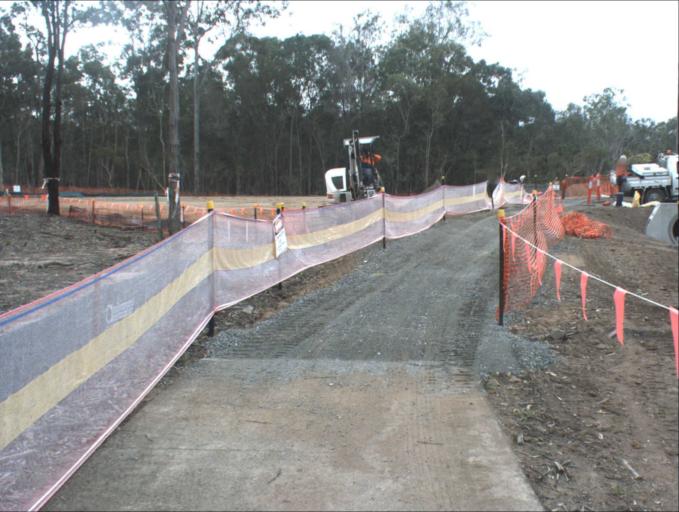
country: AU
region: Queensland
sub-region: Logan
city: Woodridge
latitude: -27.6734
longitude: 153.0723
